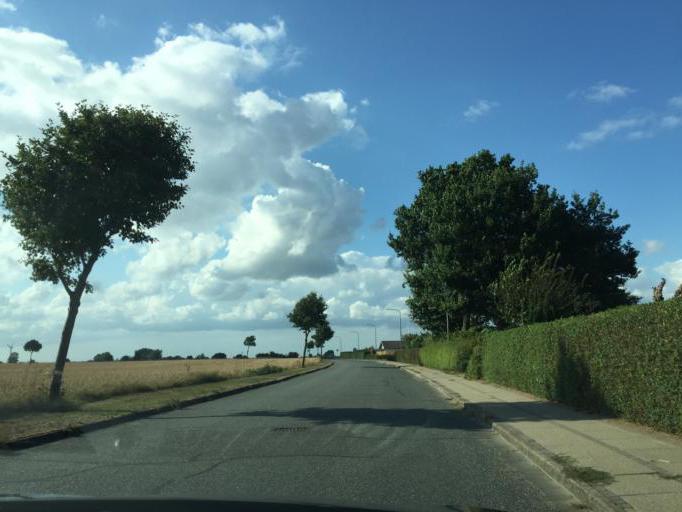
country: DK
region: South Denmark
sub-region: Faaborg-Midtfyn Kommune
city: Arslev
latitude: 55.3081
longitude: 10.4777
